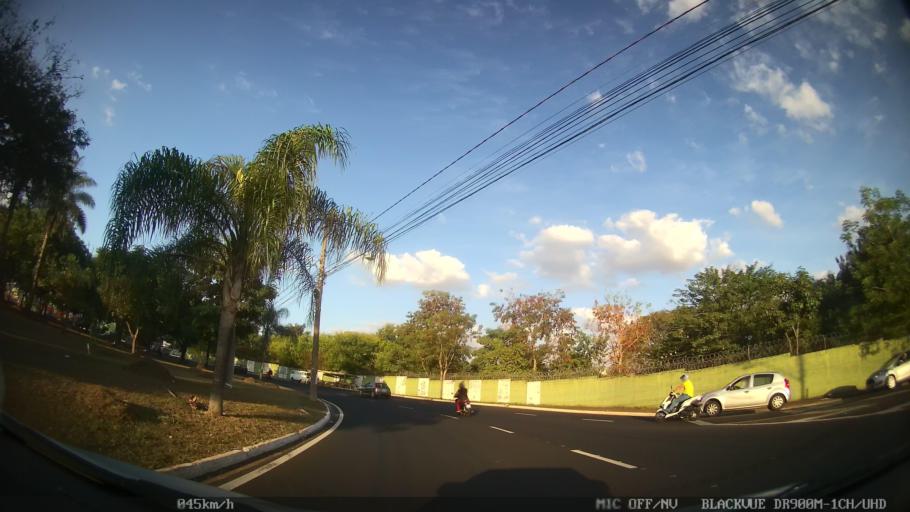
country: BR
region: Sao Paulo
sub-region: Ribeirao Preto
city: Ribeirao Preto
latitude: -21.1384
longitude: -47.7979
